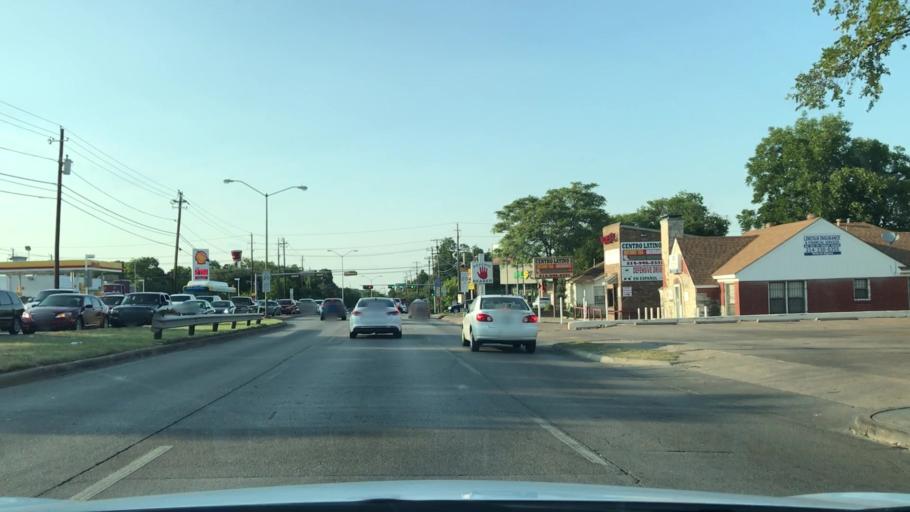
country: US
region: Texas
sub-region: Dallas County
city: Cockrell Hill
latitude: 32.7481
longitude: -96.8567
